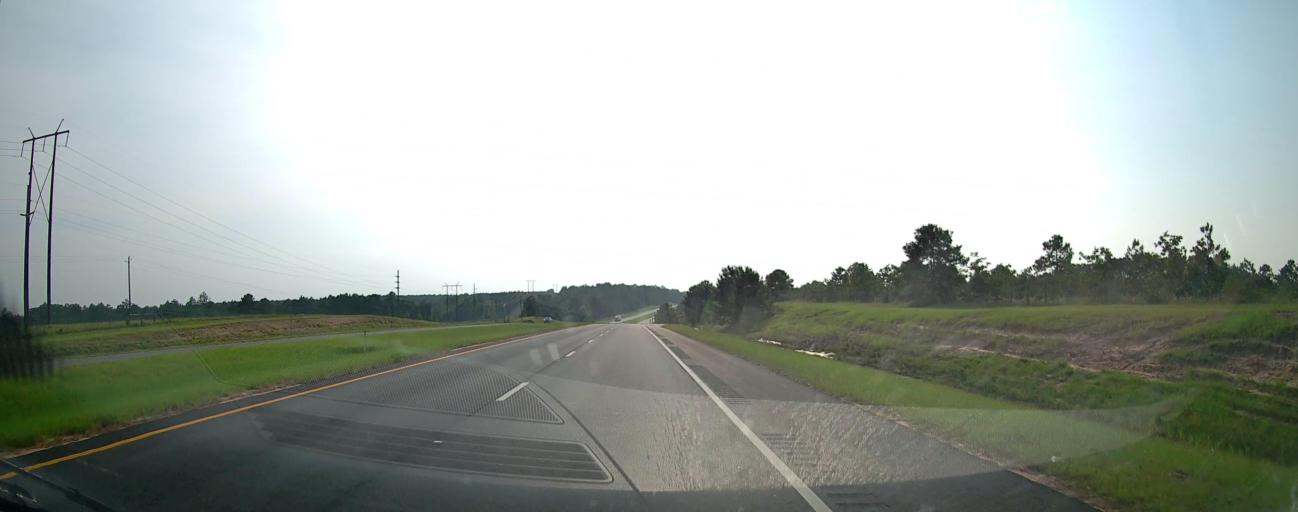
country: US
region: Georgia
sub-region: Taylor County
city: Butler
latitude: 32.5926
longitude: -84.3902
